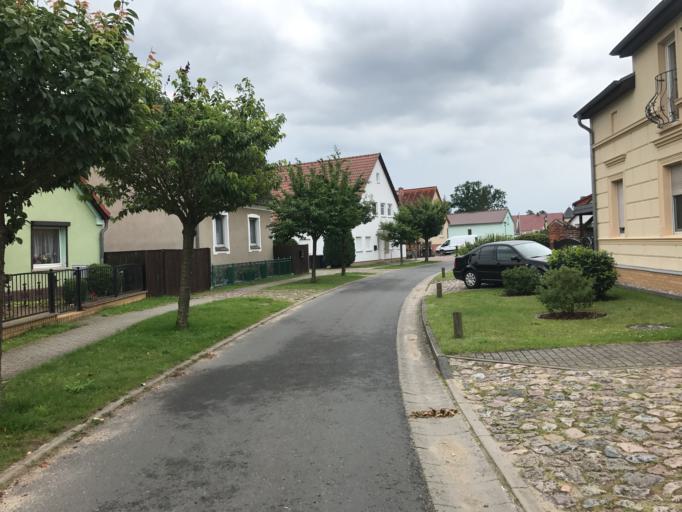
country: DE
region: Brandenburg
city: Melchow
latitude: 52.8491
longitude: 13.6839
